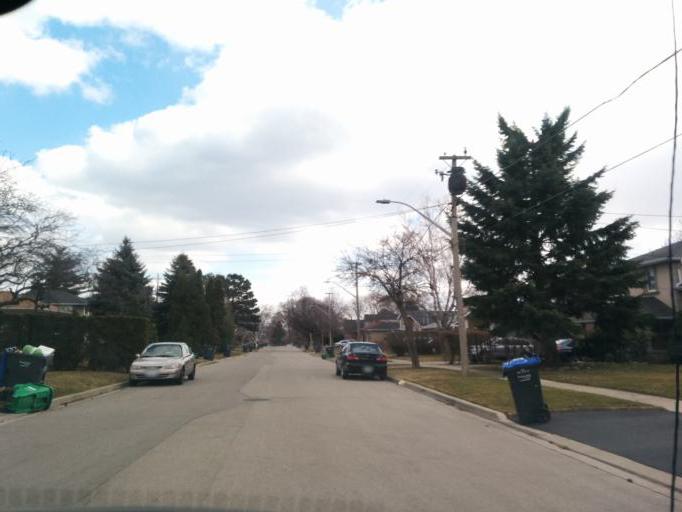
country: CA
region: Ontario
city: Etobicoke
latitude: 43.5887
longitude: -79.5735
